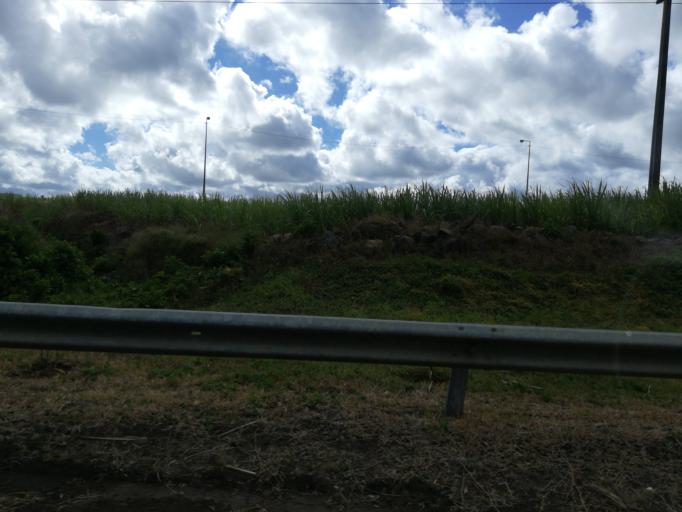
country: MU
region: Grand Port
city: Plaine Magnien
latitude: -20.4276
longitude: 57.6491
